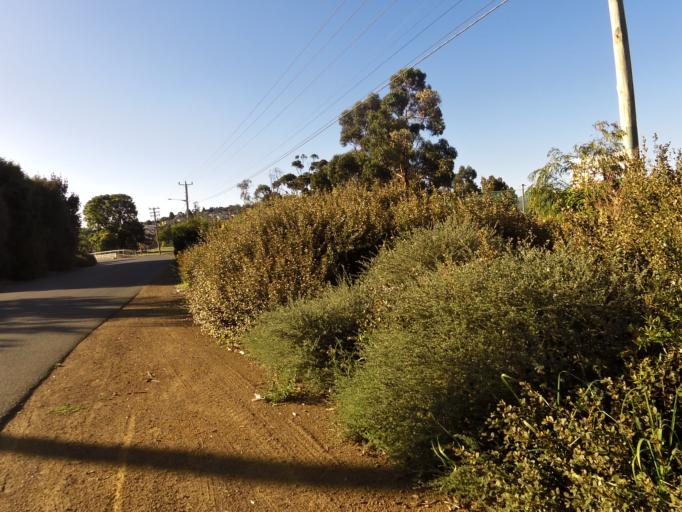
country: AU
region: Tasmania
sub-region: Hobart
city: New Town
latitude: -42.8500
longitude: 147.3138
